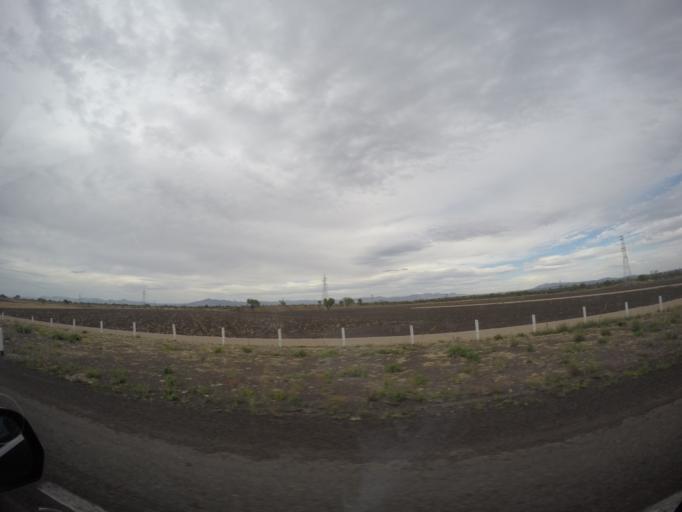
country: MX
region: Guanajuato
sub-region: Irapuato
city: Serrano
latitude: 20.8169
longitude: -101.4415
